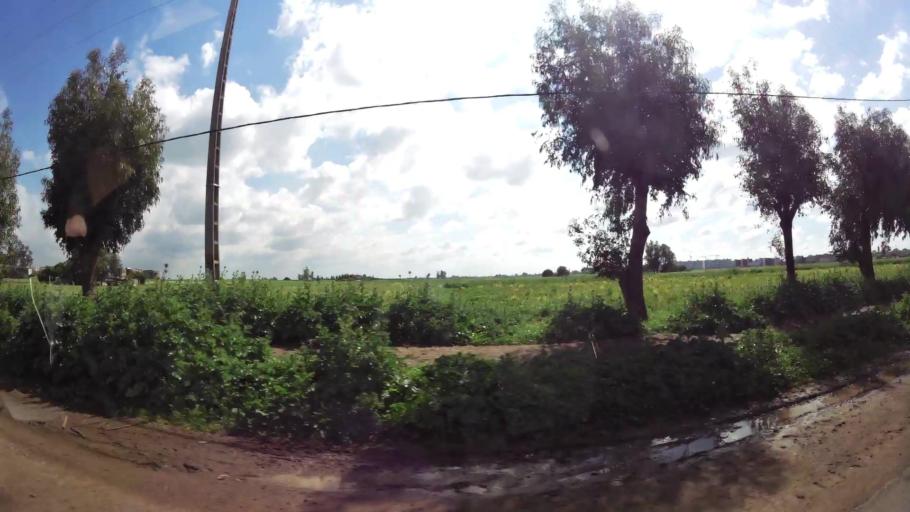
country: MA
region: Grand Casablanca
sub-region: Mediouna
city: Mediouna
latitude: 33.4475
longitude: -7.5043
